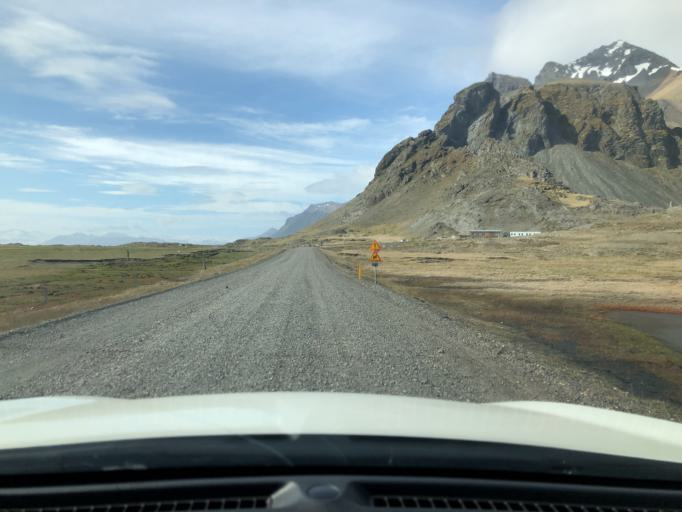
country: IS
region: East
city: Hoefn
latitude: 64.2528
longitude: -14.9909
